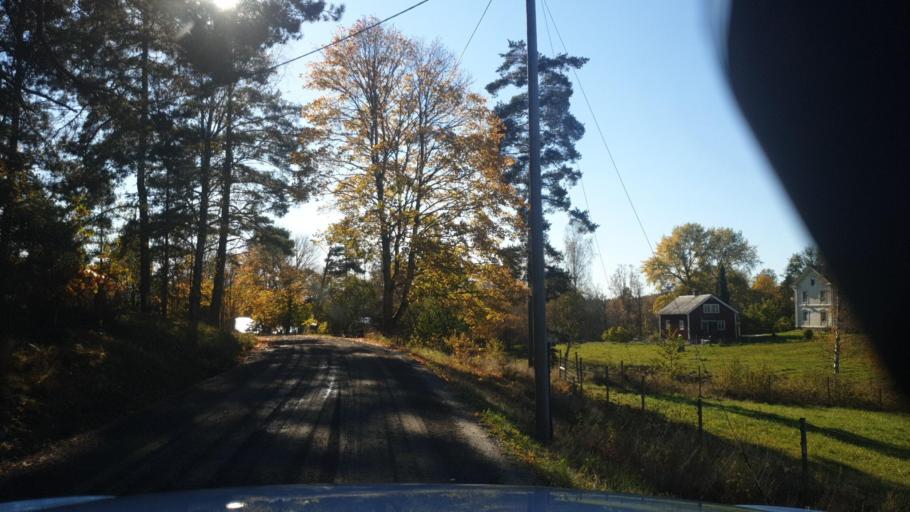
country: SE
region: Vaermland
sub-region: Grums Kommun
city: Slottsbron
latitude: 59.4567
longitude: 12.9173
